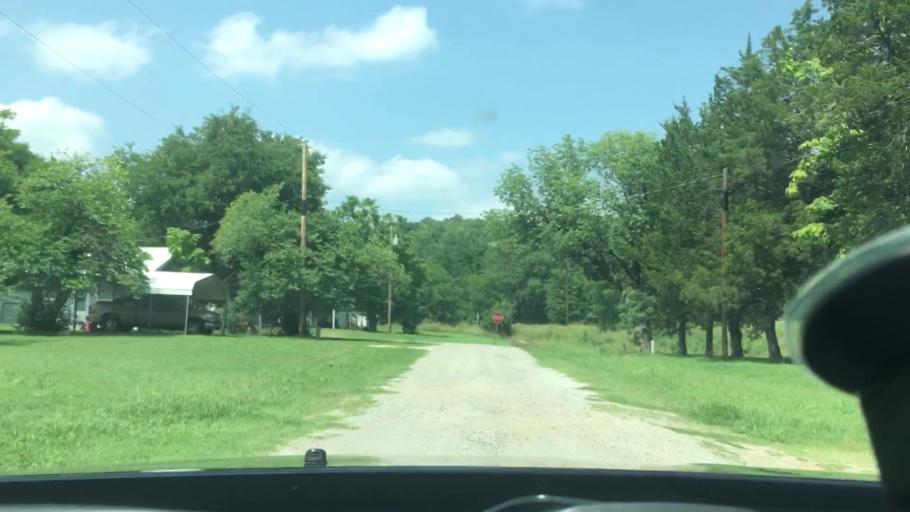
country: US
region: Oklahoma
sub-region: Johnston County
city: Tishomingo
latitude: 34.4178
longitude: -96.4957
